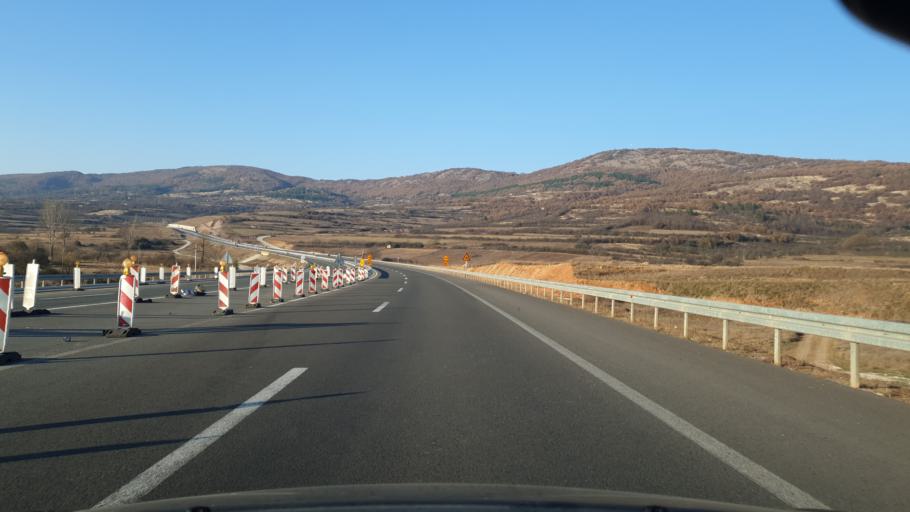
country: RS
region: Central Serbia
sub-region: Pirotski Okrug
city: Dimitrovgrad
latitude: 43.0121
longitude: 22.8030
